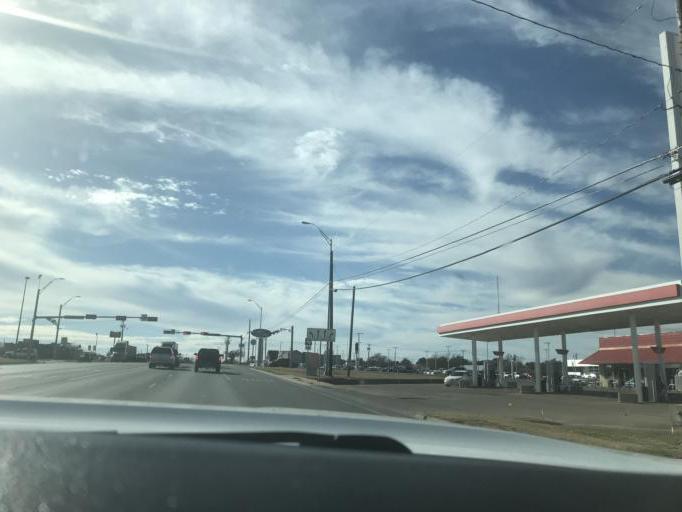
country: US
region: Texas
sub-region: Erath County
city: Stephenville
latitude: 32.2020
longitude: -98.2451
